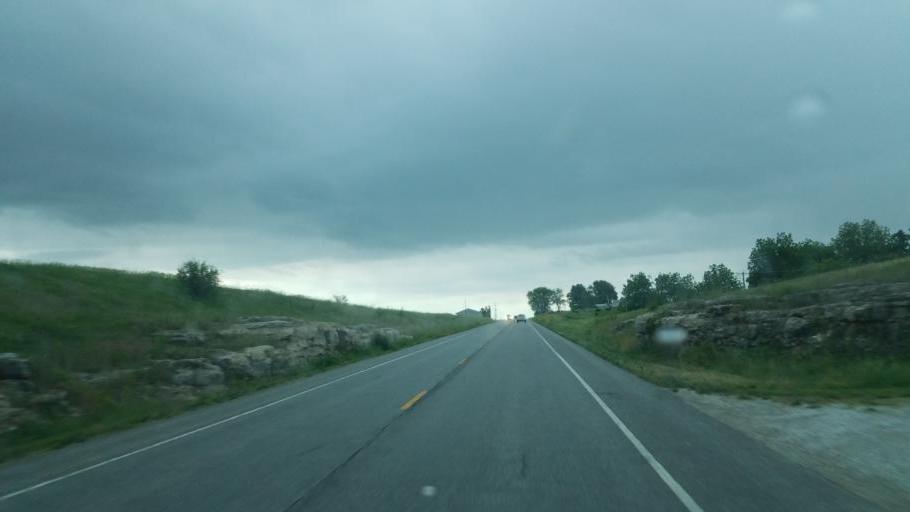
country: US
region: Missouri
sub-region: Cooper County
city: Boonville
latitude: 38.9174
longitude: -92.6857
